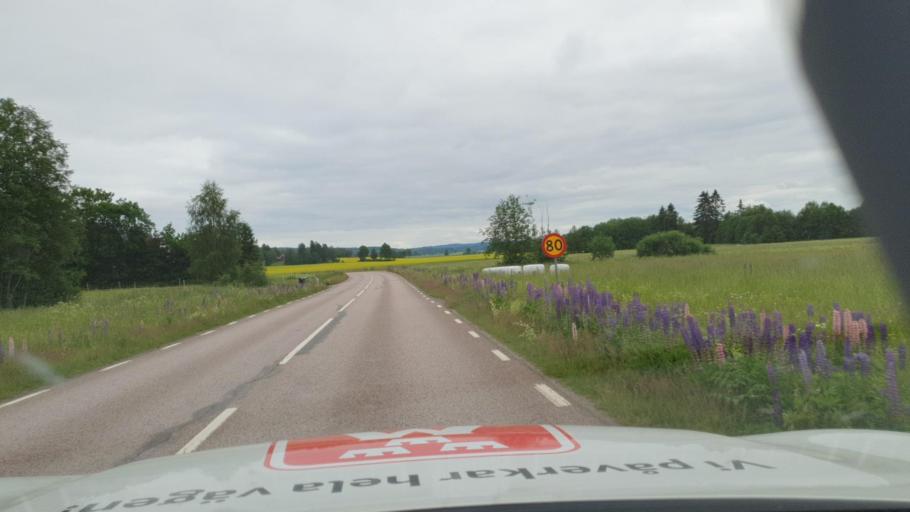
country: SE
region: Vaermland
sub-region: Sunne Kommun
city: Sunne
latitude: 59.7928
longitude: 13.2288
